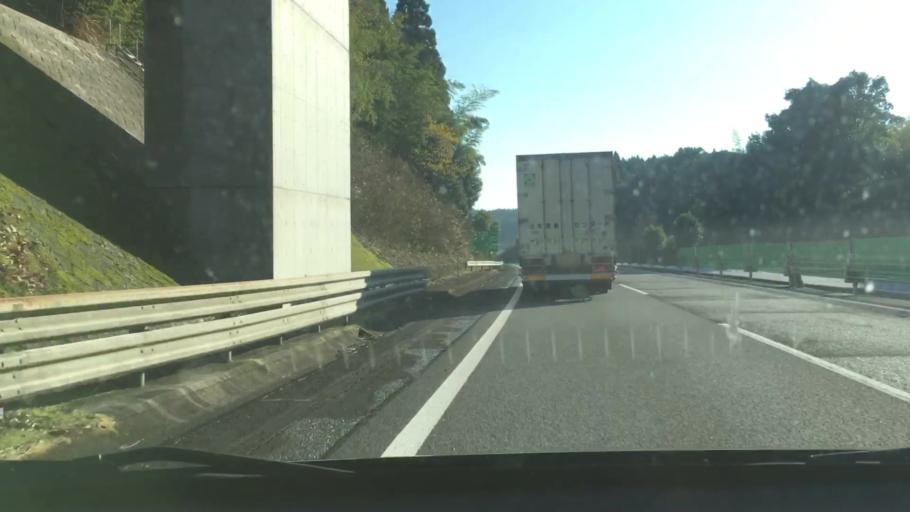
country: JP
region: Kagoshima
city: Kajiki
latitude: 31.8861
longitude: 130.6959
